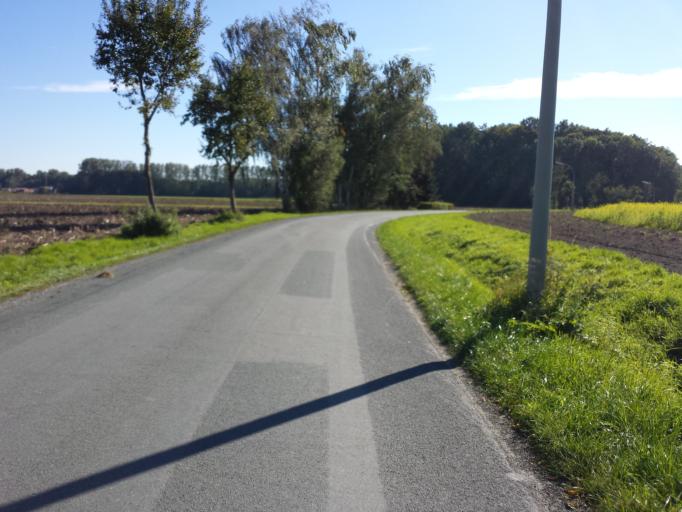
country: DE
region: North Rhine-Westphalia
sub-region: Regierungsbezirk Detmold
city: Langenberg
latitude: 51.7941
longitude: 8.3302
